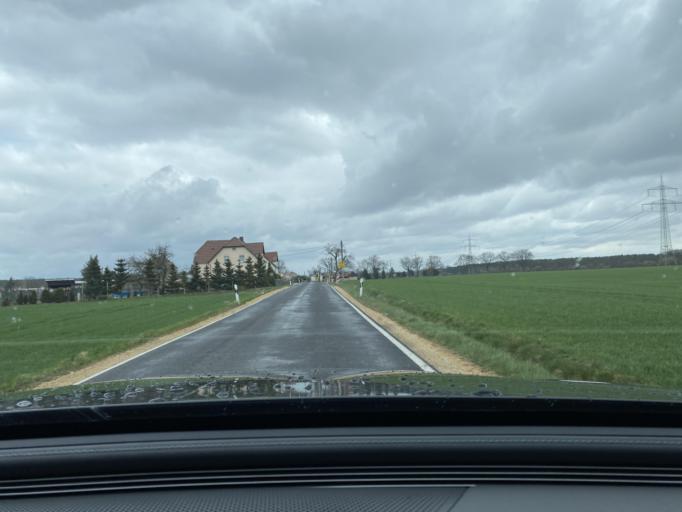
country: DE
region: Saxony
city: Radibor
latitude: 51.2693
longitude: 14.4305
